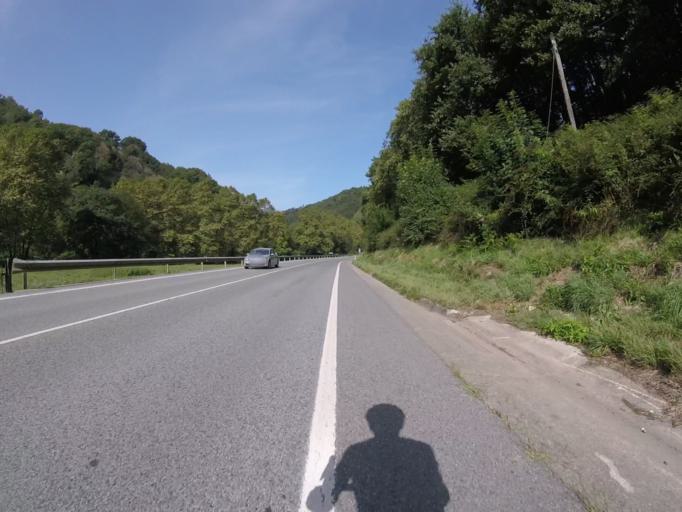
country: ES
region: Navarre
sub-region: Provincia de Navarra
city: Doneztebe
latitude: 43.1408
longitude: -1.5790
